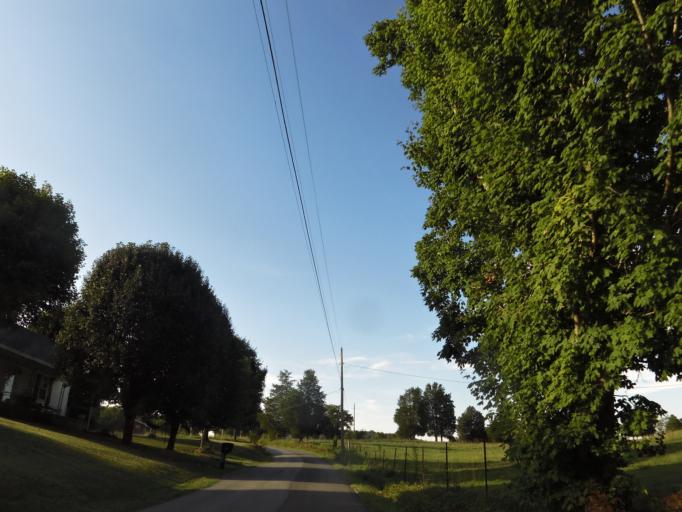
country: US
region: Tennessee
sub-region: Blount County
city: Eagleton Village
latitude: 35.8566
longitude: -83.9176
